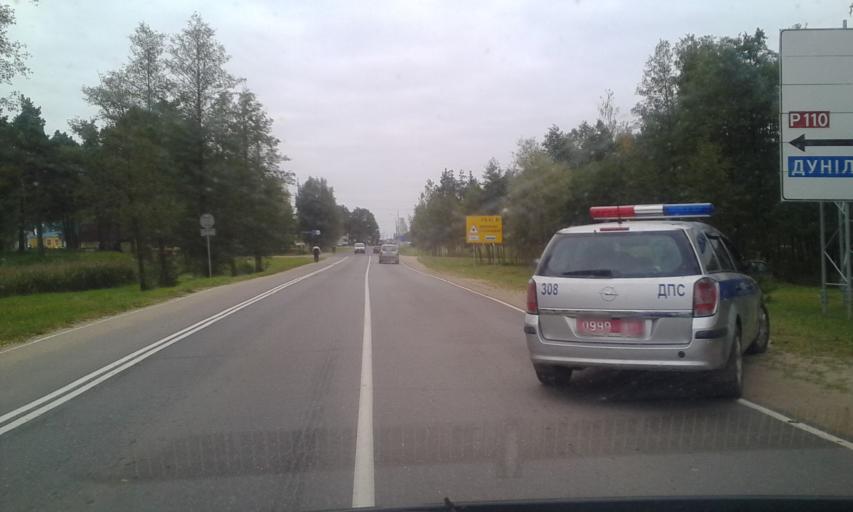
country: BY
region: Vitebsk
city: Pastavy
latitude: 55.1158
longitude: 26.8718
